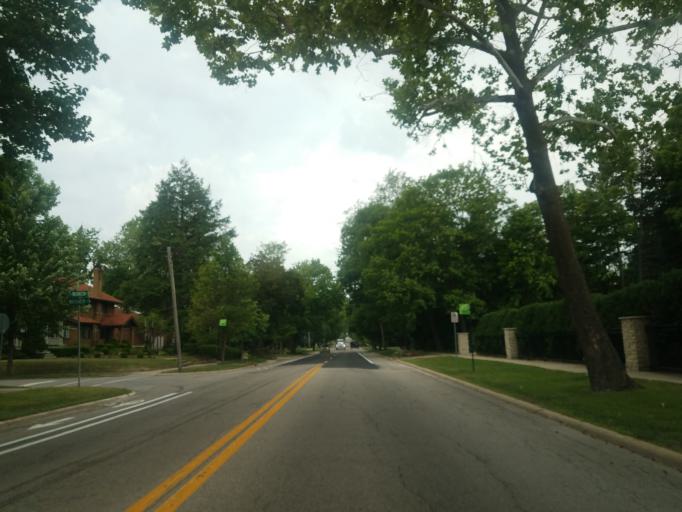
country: US
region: Illinois
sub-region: McLean County
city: Bloomington
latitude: 40.4801
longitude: -88.9636
